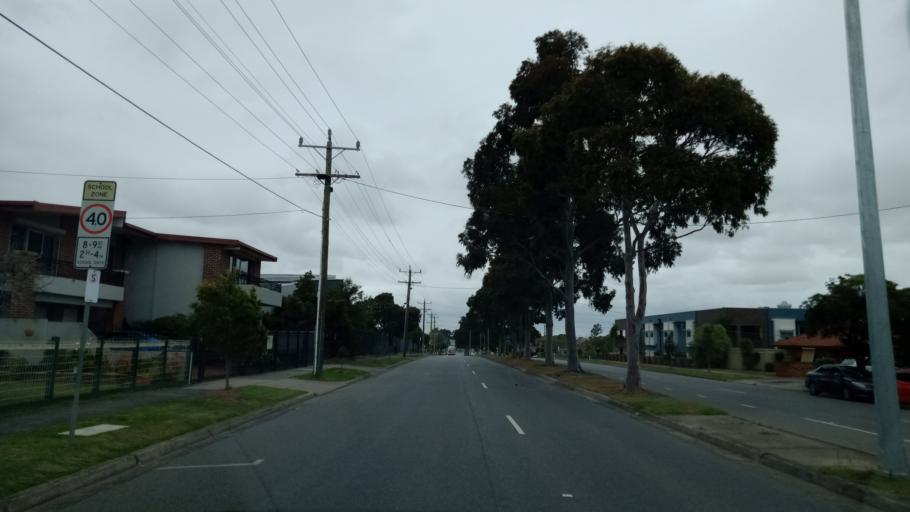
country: AU
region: Victoria
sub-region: Casey
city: Doveton
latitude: -37.9901
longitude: 145.2195
